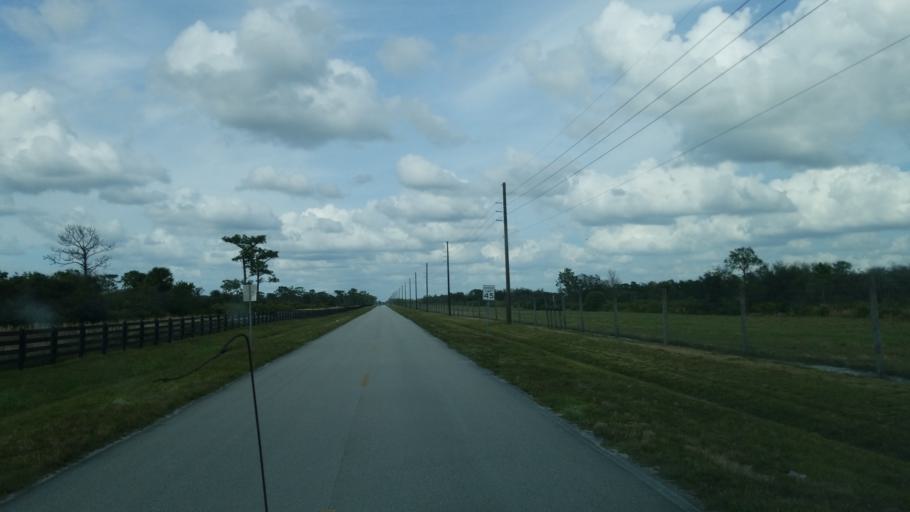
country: US
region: Florida
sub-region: Okeechobee County
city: Cypress Quarters
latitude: 27.4875
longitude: -80.7732
